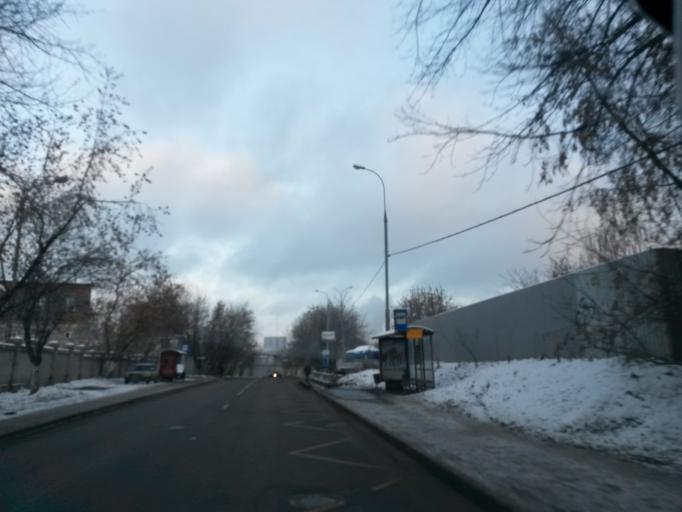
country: RU
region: Moscow
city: Amin'yevo
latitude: 55.7058
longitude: 37.4484
